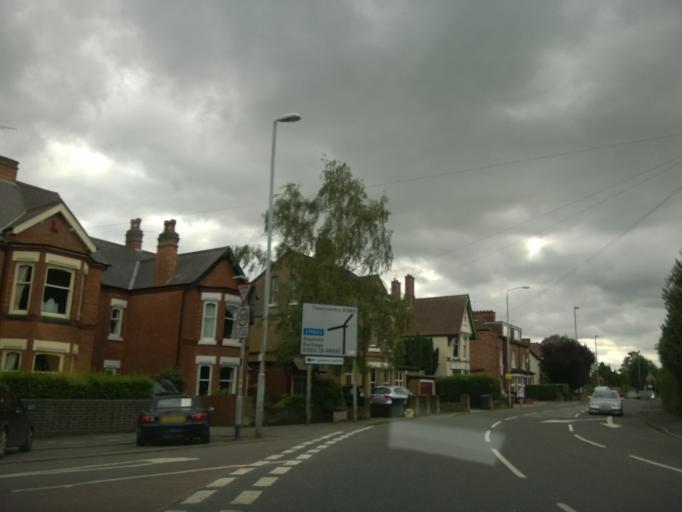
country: GB
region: England
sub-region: Leicestershire
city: Hinckley
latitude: 52.5448
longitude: -1.3634
